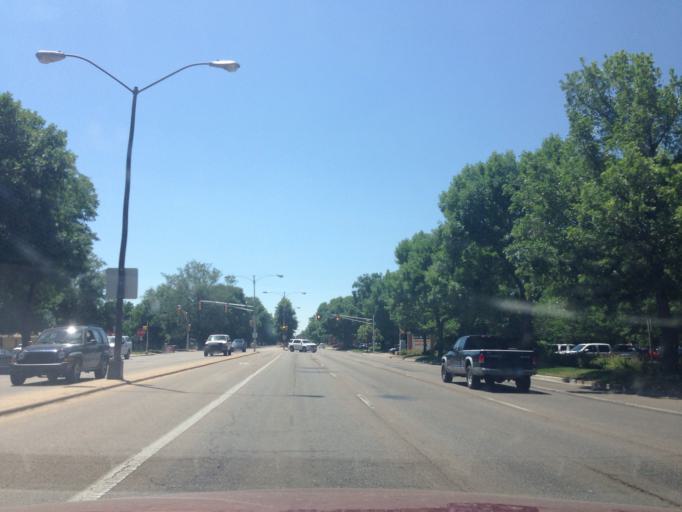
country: US
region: Colorado
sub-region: Larimer County
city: Fort Collins
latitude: 40.5584
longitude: -105.0771
